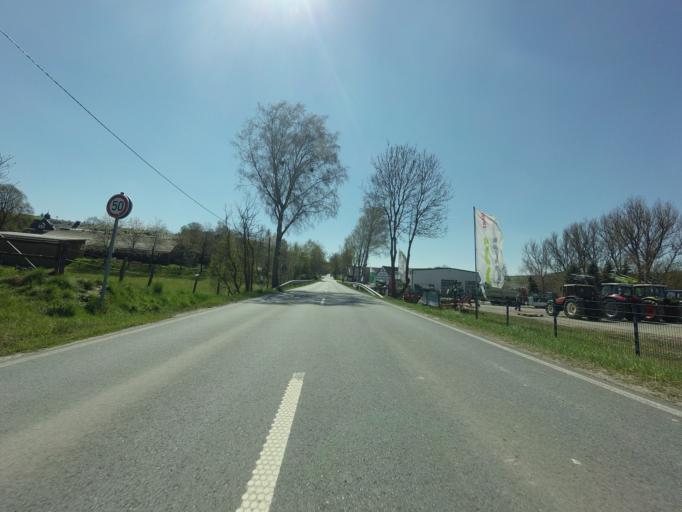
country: DE
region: North Rhine-Westphalia
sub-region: Regierungsbezirk Arnsberg
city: Erndtebruck
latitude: 51.0108
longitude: 8.2602
